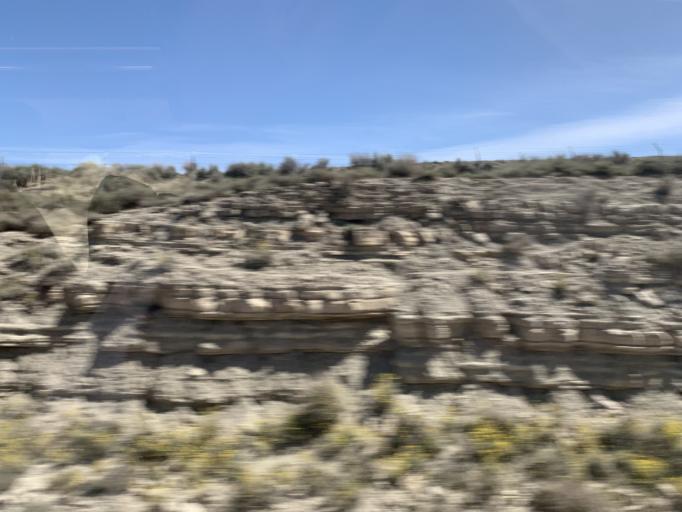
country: ES
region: Aragon
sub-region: Provincia de Huesca
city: Penalba
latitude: 41.5280
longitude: -0.0644
